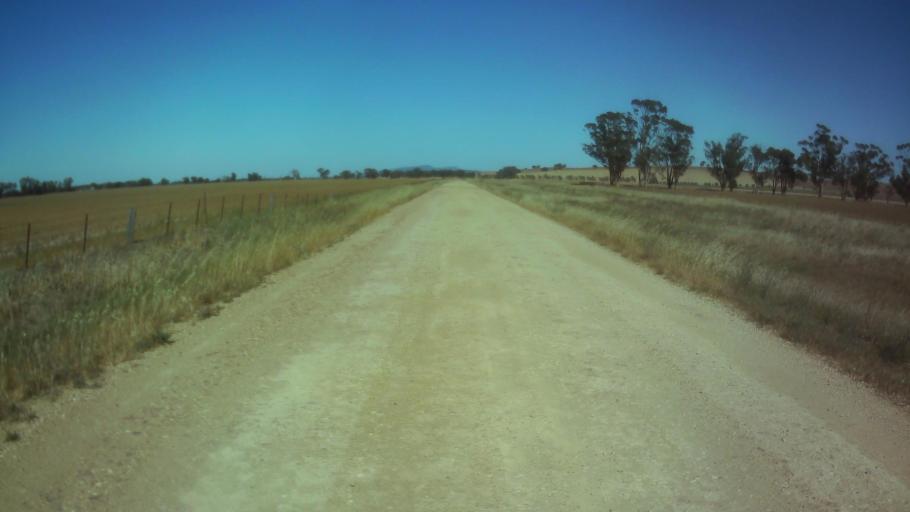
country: AU
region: New South Wales
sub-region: Weddin
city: Grenfell
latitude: -33.9959
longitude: 148.3740
